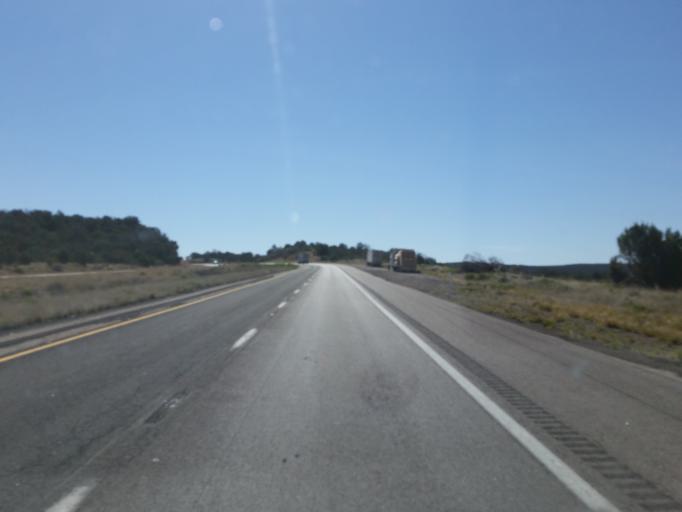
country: US
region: Arizona
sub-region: Mohave County
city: Peach Springs
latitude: 35.2860
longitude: -113.1022
